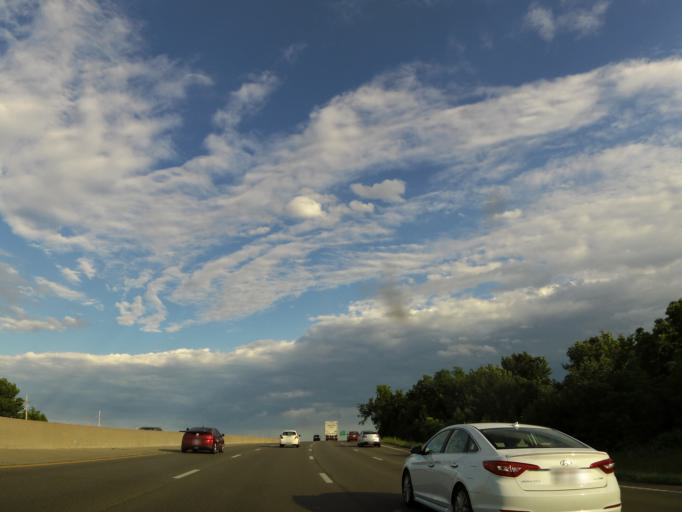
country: US
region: Missouri
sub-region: Saint Charles County
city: Weldon Spring
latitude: 38.7083
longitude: -90.6769
